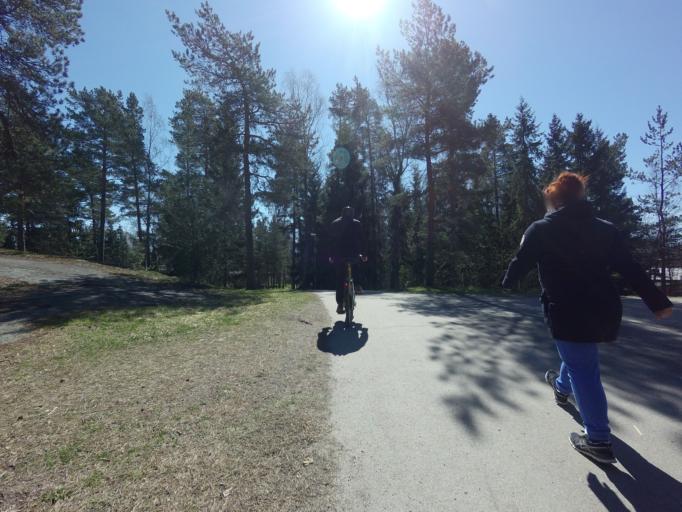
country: FI
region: Uusimaa
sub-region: Helsinki
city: Koukkuniemi
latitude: 60.1502
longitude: 24.7465
